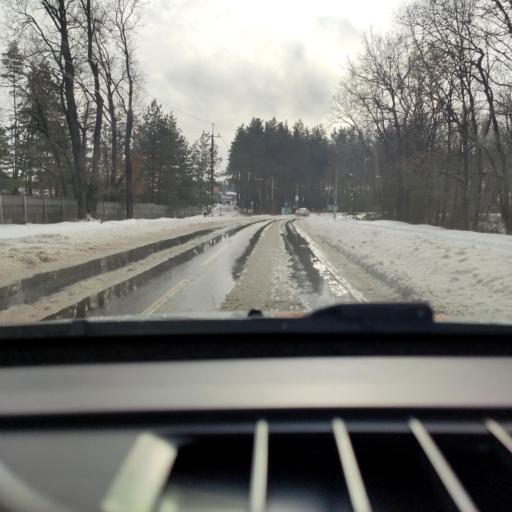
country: RU
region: Voronezj
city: Podgornoye
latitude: 51.7869
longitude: 39.1462
